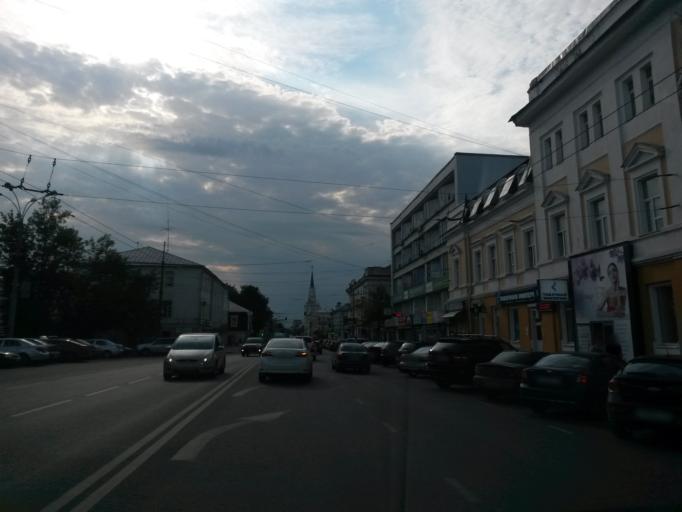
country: RU
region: Jaroslavl
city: Yaroslavl
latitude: 57.6257
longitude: 39.8747
